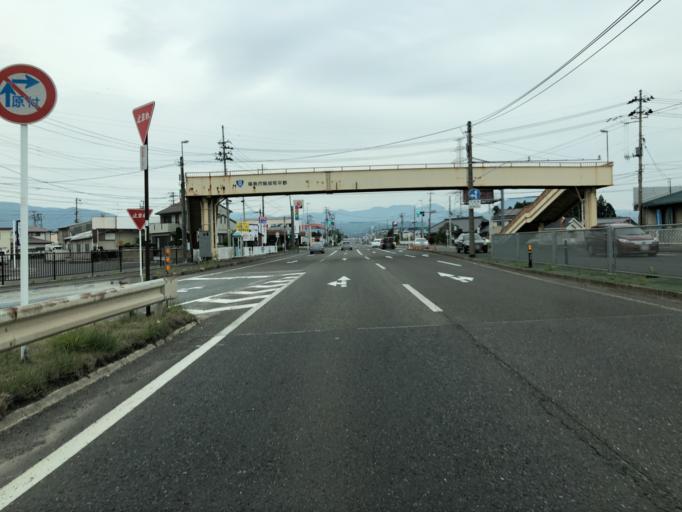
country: JP
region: Fukushima
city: Fukushima-shi
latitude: 37.8054
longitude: 140.4509
